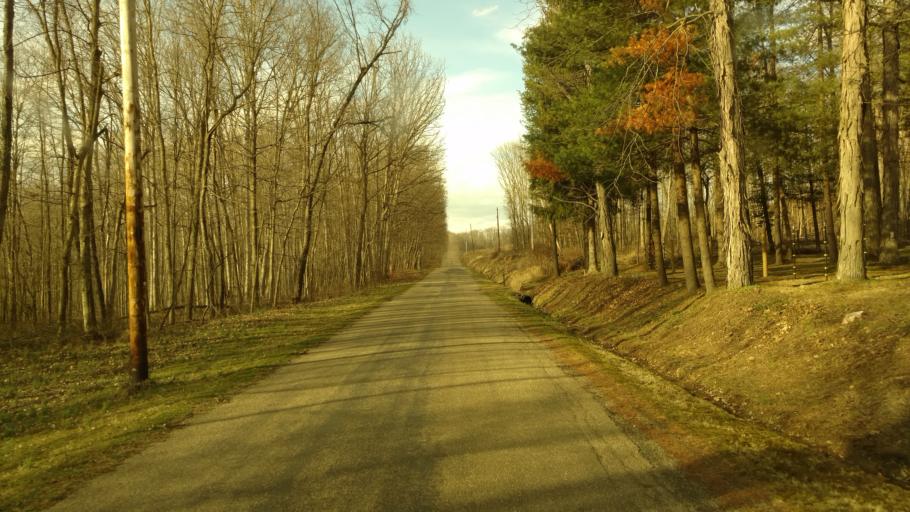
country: US
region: Ohio
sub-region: Sandusky County
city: Bellville
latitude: 40.5655
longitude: -82.4331
